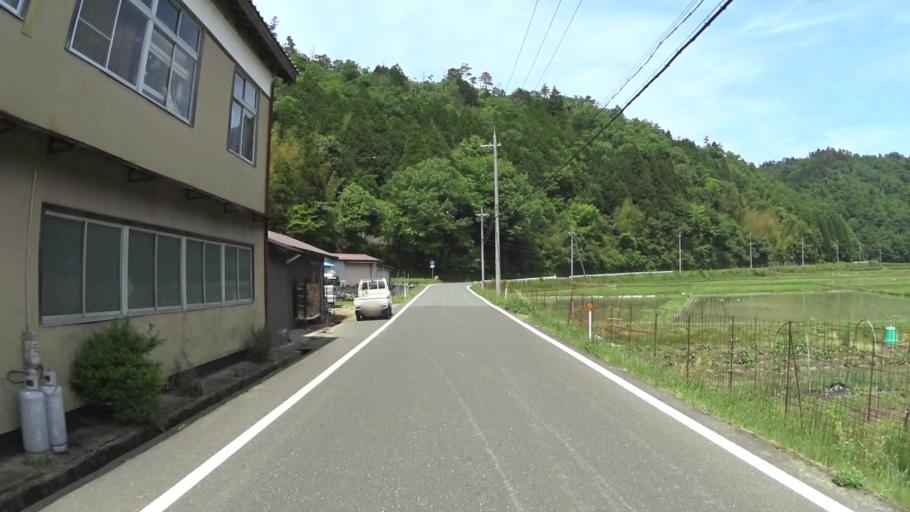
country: JP
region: Kyoto
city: Maizuru
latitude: 35.3889
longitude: 135.4622
